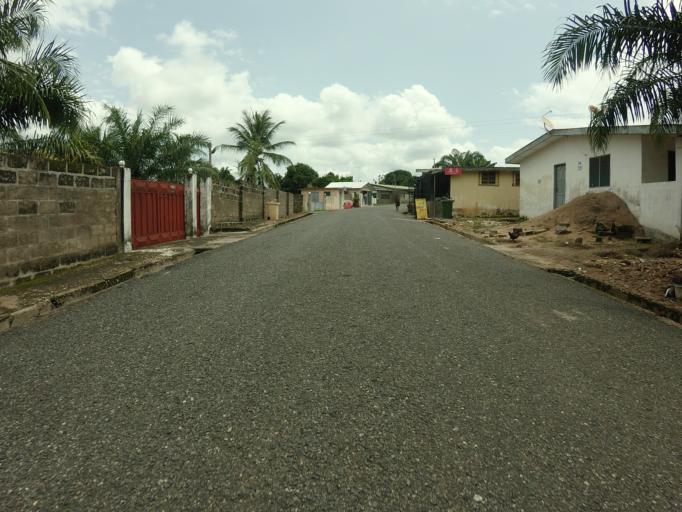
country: GH
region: Volta
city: Ho
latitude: 6.5913
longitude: 0.4755
